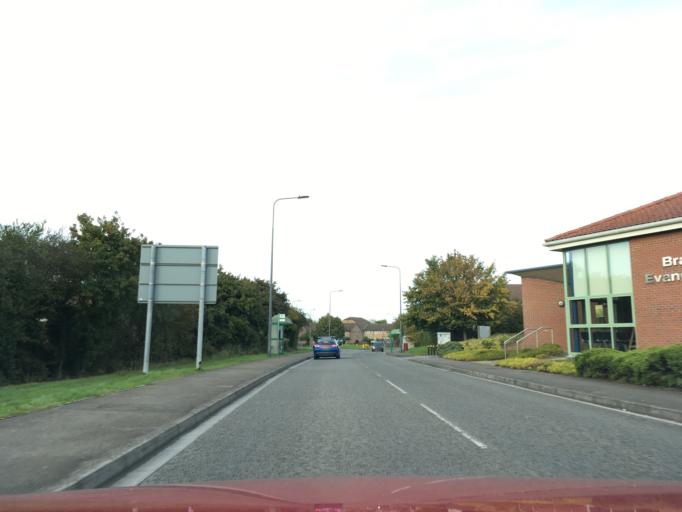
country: GB
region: England
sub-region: South Gloucestershire
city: Stoke Gifford
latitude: 51.5259
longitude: -2.5332
